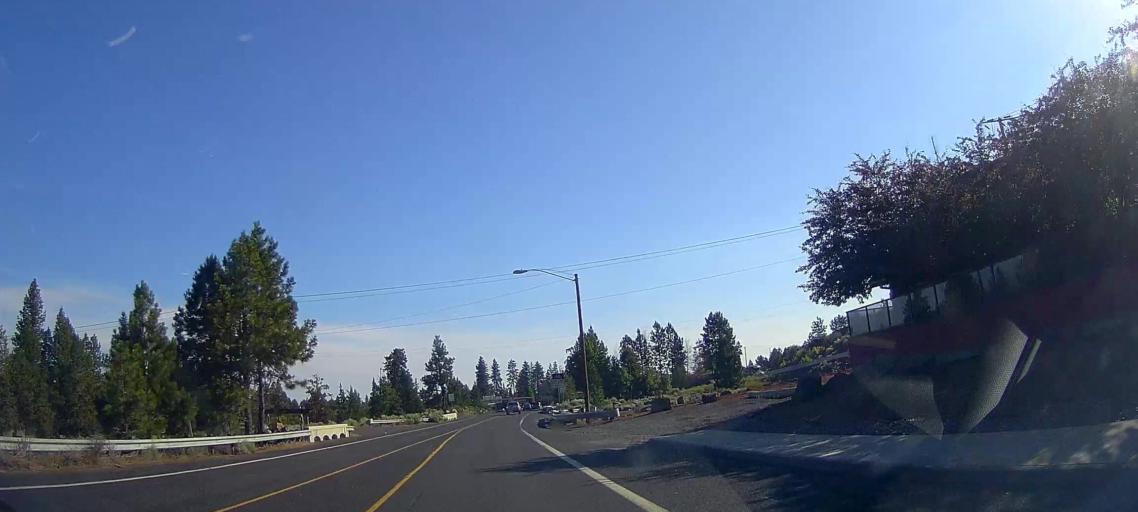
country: US
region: Oregon
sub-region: Deschutes County
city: Bend
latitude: 44.0760
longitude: -121.3054
